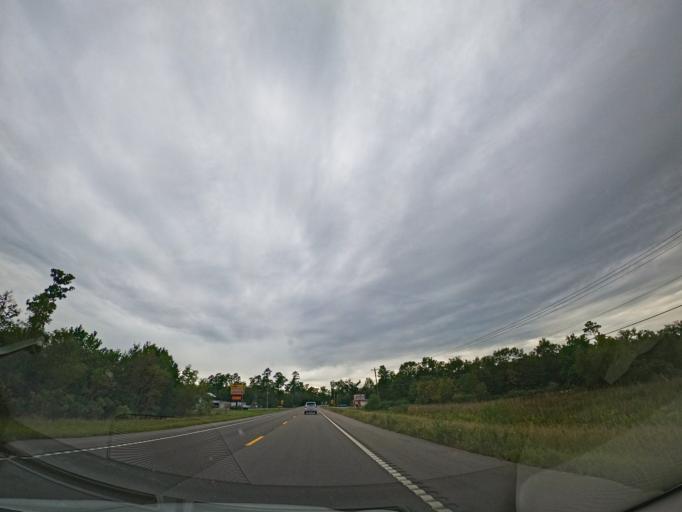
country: US
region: Mississippi
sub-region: Hancock County
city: Pearlington
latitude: 30.2415
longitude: -89.6070
